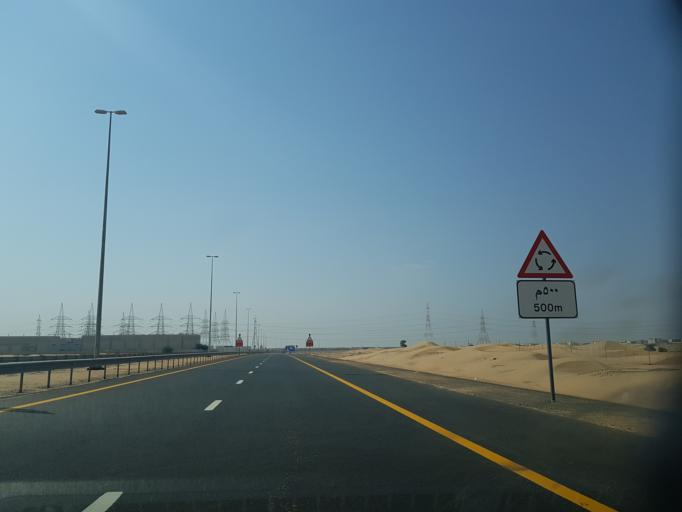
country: AE
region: Ash Shariqah
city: Sharjah
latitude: 25.2842
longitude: 55.5964
